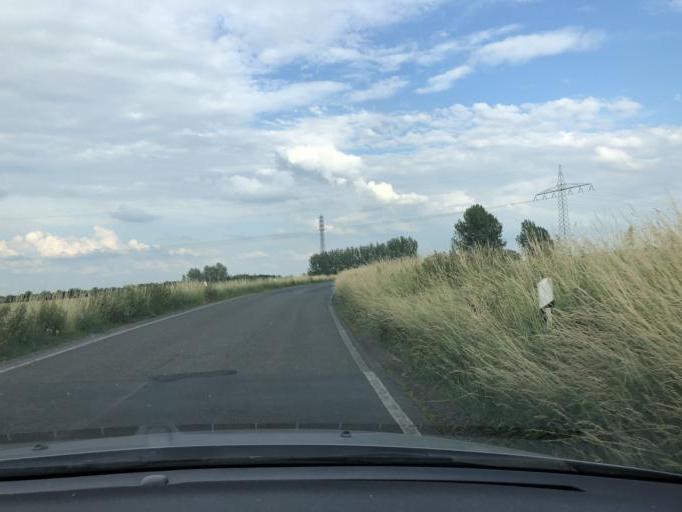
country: DE
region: Saxony
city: Wilsdruff
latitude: 51.0547
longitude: 13.5961
